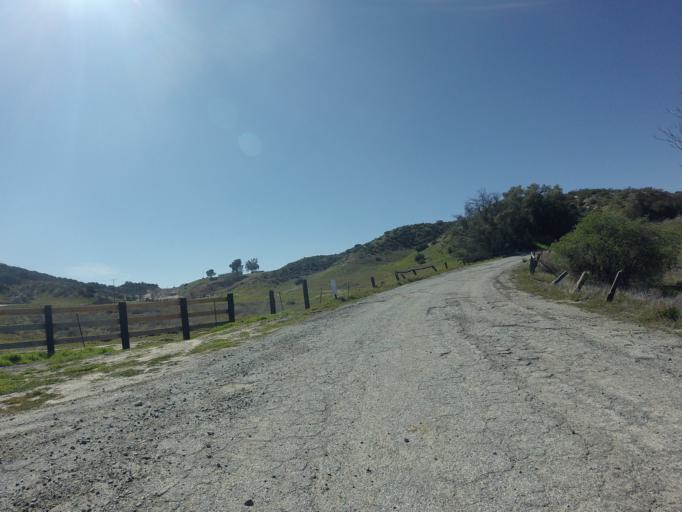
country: US
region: California
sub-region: Riverside County
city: Beaumont
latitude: 33.9312
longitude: -117.0348
